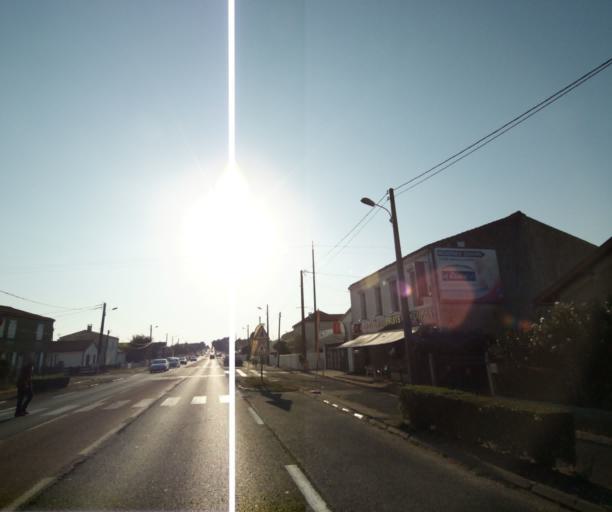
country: FR
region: Poitou-Charentes
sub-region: Departement de la Charente-Maritime
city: Tonnay-Charente
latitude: 45.9498
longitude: -0.9236
